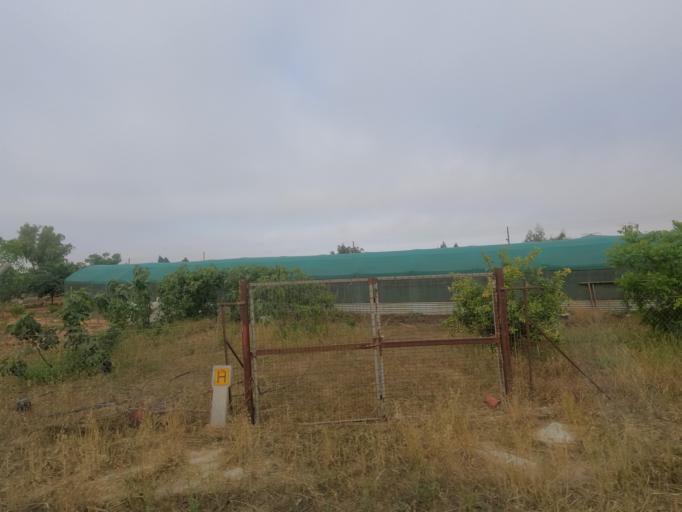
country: CY
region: Ammochostos
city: Achna
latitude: 35.0403
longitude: 33.7908
